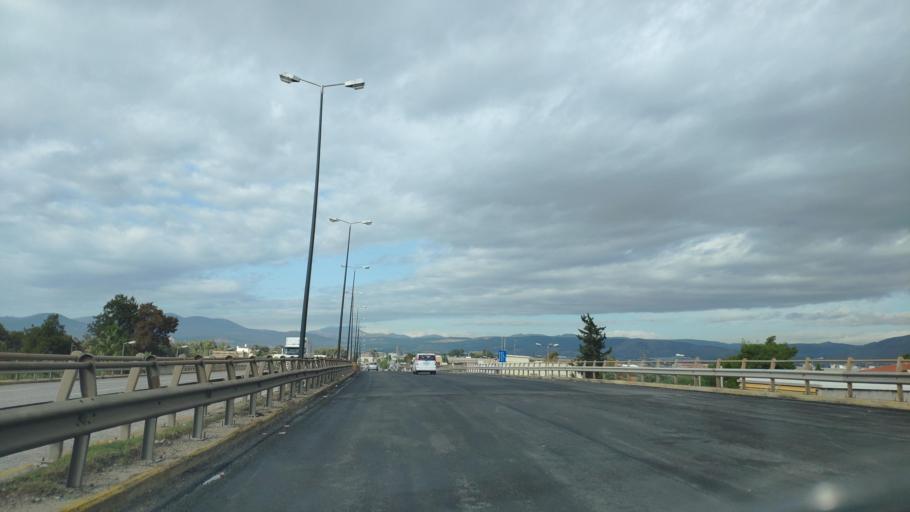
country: GR
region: Attica
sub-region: Nomarchia Dytikis Attikis
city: Aspropyrgos
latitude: 38.0428
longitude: 23.5851
